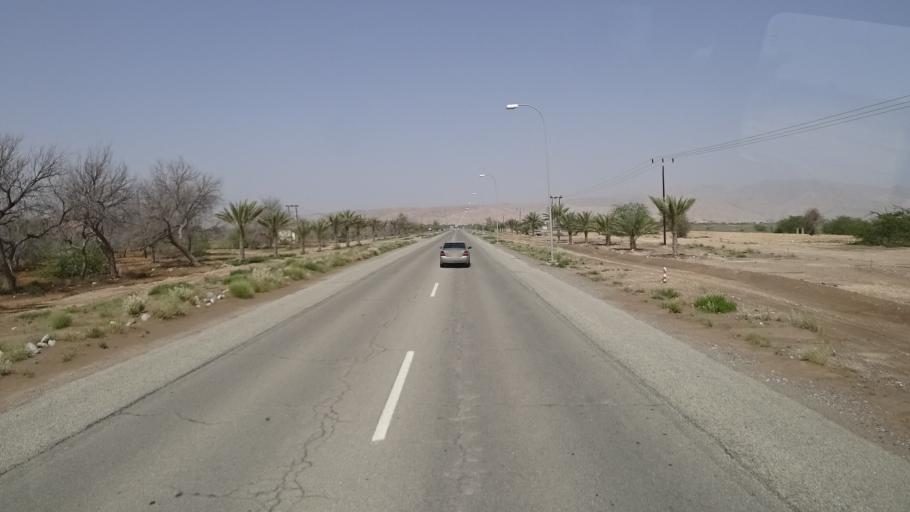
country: OM
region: Muhafazat Masqat
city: Muscat
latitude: 23.2153
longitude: 58.9322
